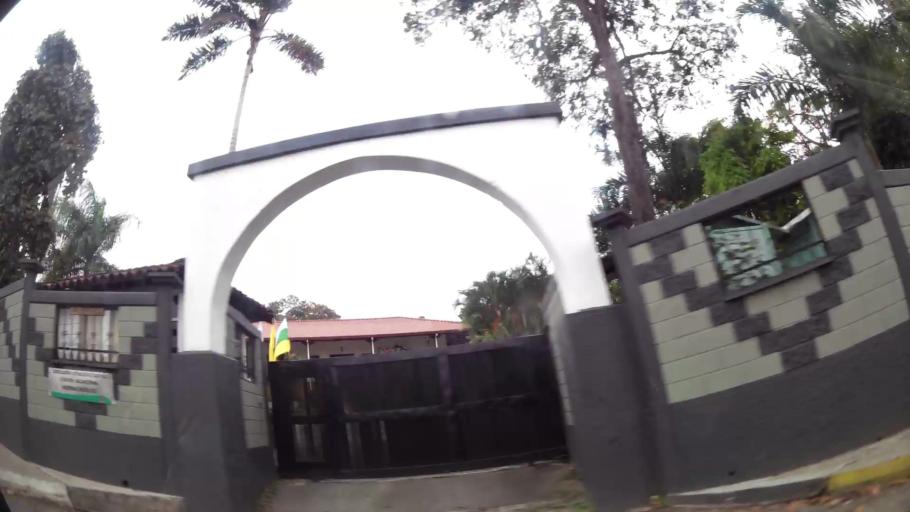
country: CO
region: Antioquia
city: Medellin
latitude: 6.2781
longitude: -75.5921
